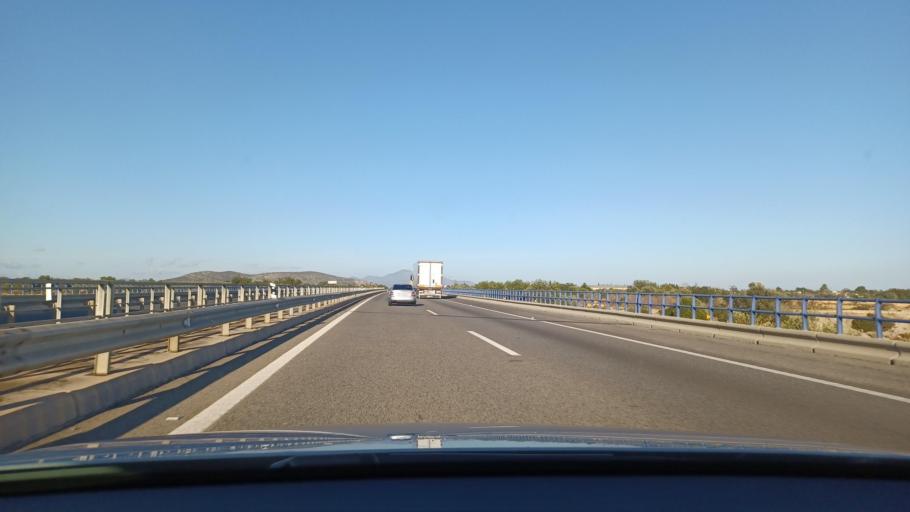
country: ES
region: Valencia
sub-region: Provincia de Castello
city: Calig
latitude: 40.4415
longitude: 0.3918
